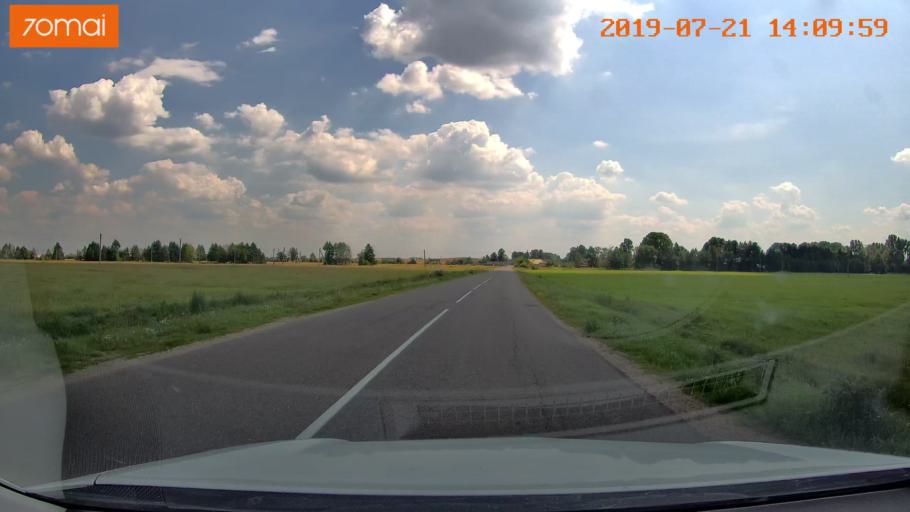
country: BY
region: Grodnenskaya
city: Karelichy
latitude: 53.6672
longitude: 26.1327
